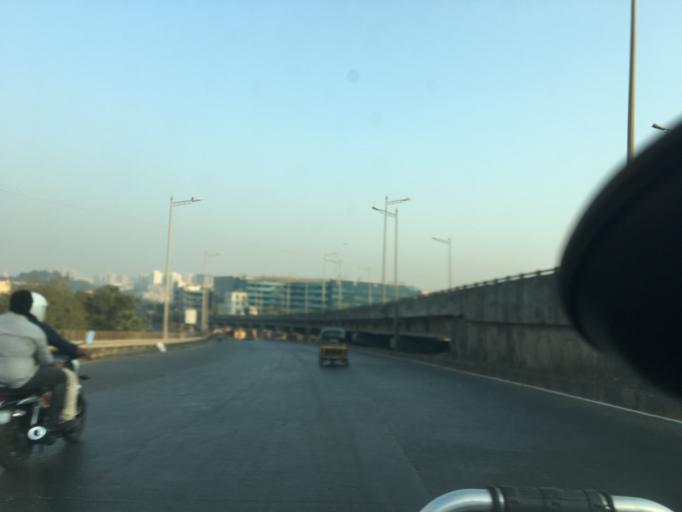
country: IN
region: Maharashtra
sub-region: Mumbai Suburban
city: Powai
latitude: 19.1310
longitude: 72.8755
